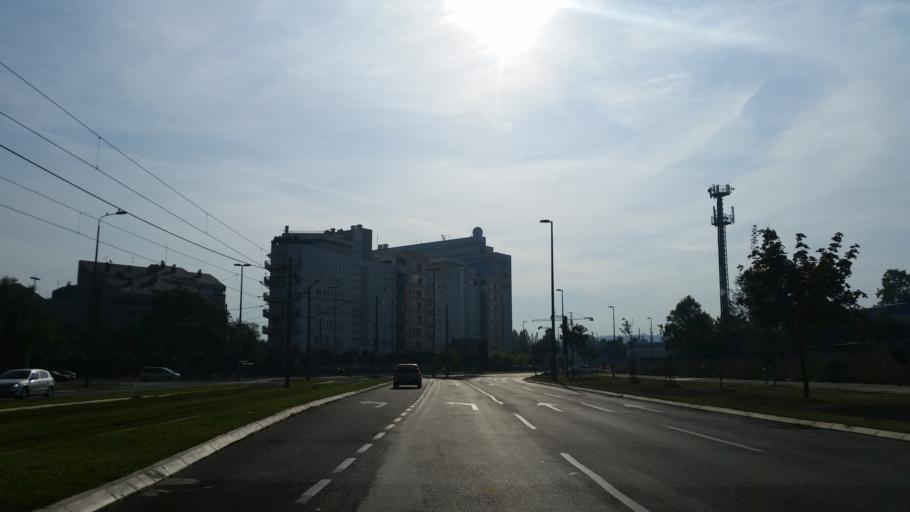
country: RS
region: Central Serbia
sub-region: Belgrade
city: Novi Beograd
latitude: 44.8057
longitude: 20.4250
